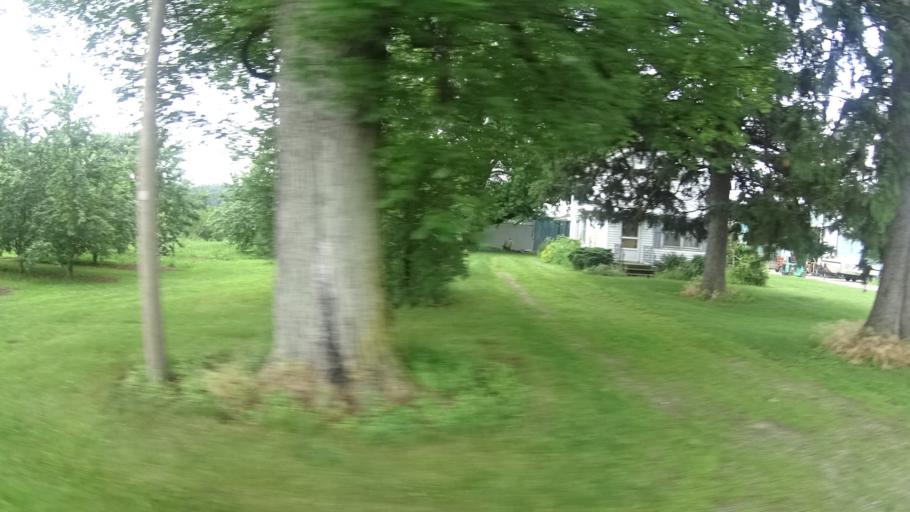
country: US
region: Ohio
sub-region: Huron County
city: Wakeman
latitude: 41.3154
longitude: -82.4815
